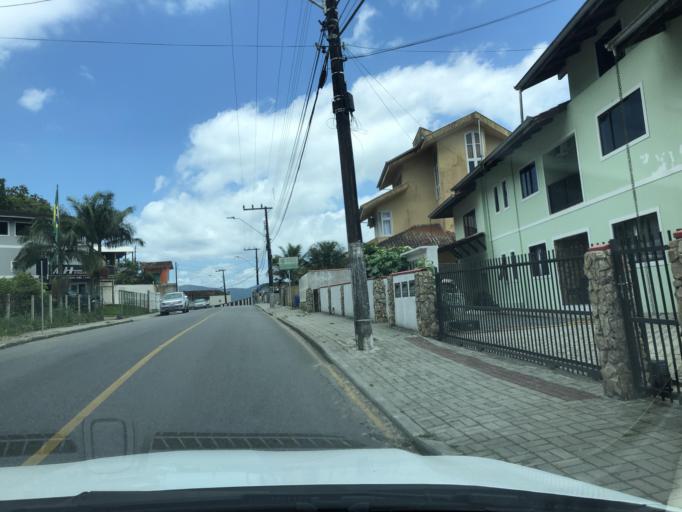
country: BR
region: Santa Catarina
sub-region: Sao Francisco Do Sul
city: Sao Francisco do Sul
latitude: -26.2306
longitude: -48.6195
